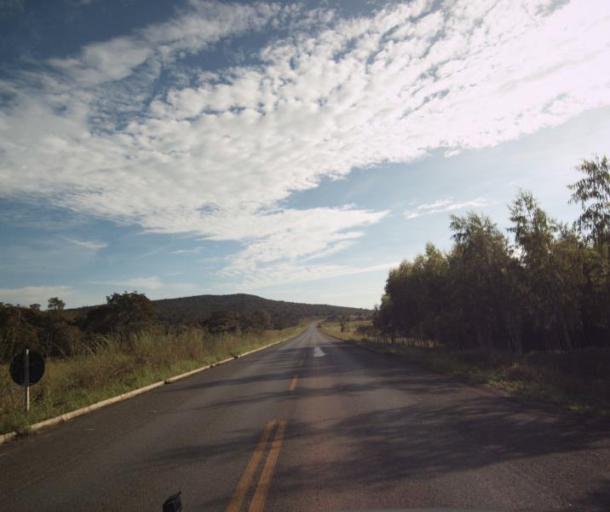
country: BR
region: Goias
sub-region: Pirenopolis
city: Pirenopolis
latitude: -15.6582
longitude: -48.6842
